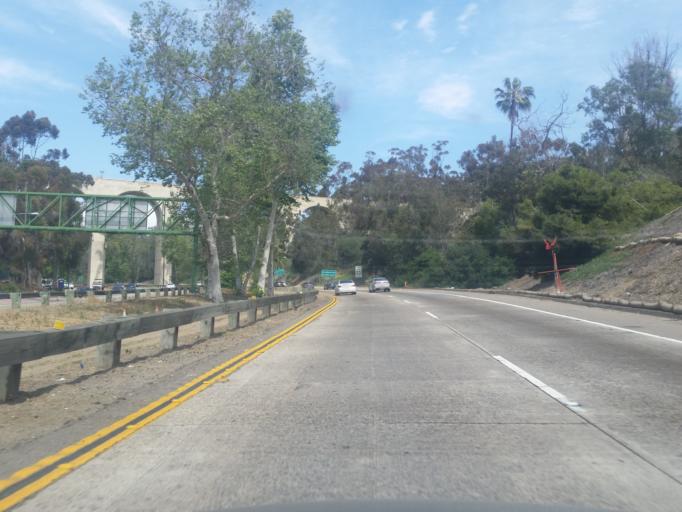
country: US
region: California
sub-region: San Diego County
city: San Diego
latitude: 32.7291
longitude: -117.1550
